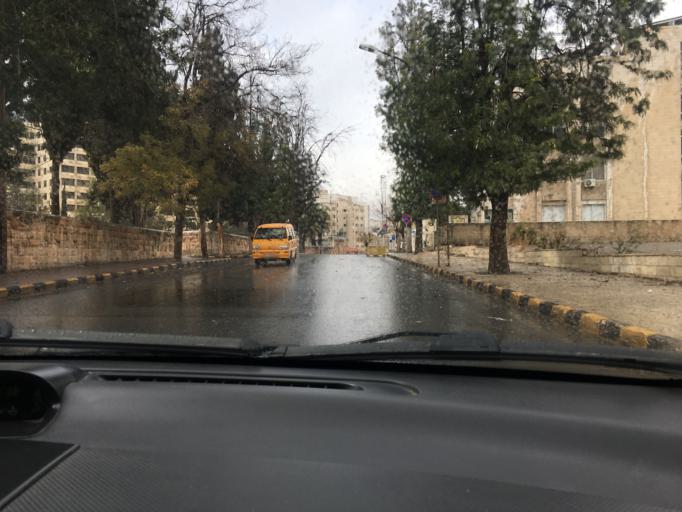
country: JO
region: Amman
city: Amman
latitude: 31.9666
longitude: 35.9123
